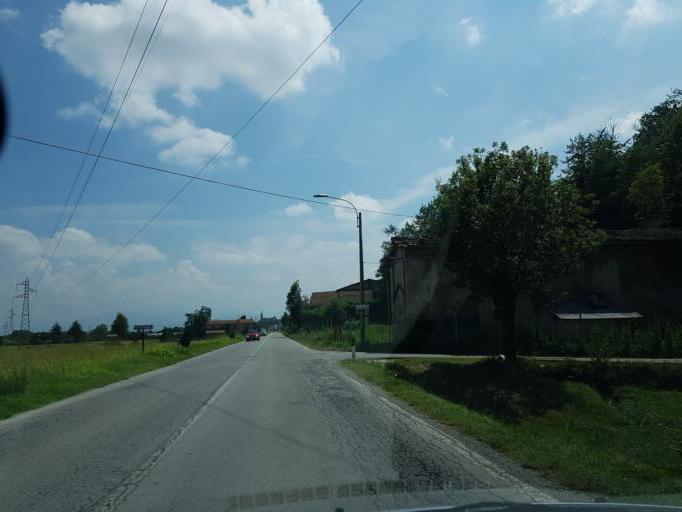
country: IT
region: Piedmont
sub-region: Provincia di Cuneo
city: Caraglio
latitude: 44.4311
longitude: 7.4237
